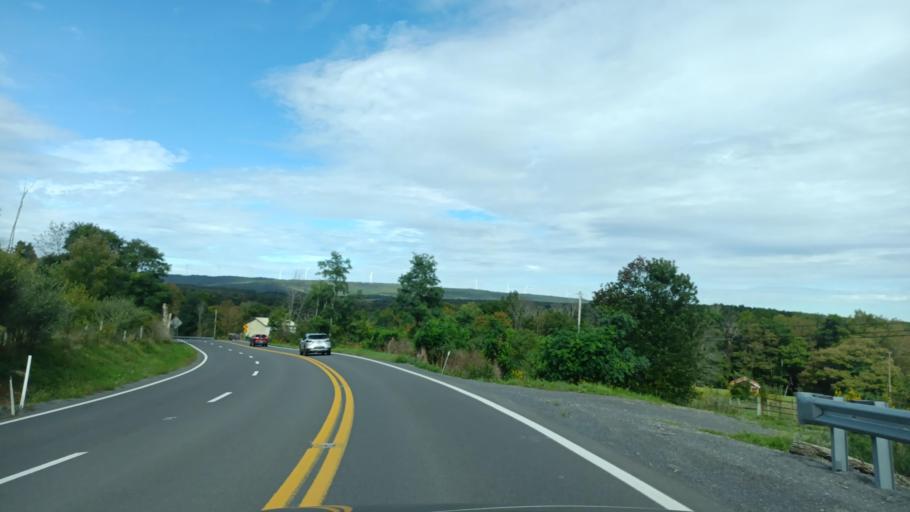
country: US
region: Maryland
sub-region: Garrett County
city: Mountain Lake Park
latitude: 39.2954
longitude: -79.3279
